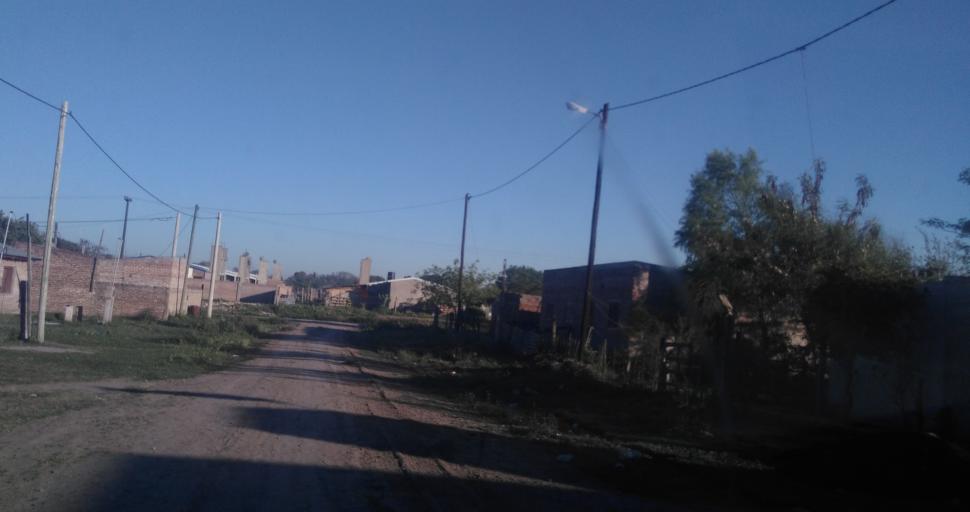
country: AR
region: Chaco
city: Fontana
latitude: -27.4220
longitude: -59.0230
